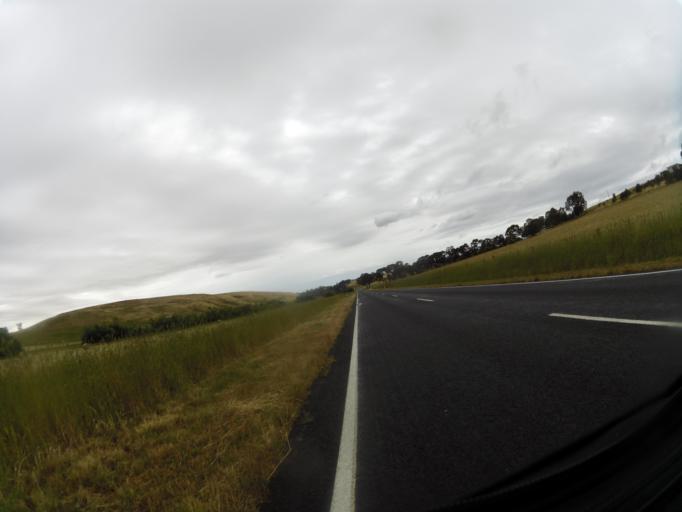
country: AU
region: Victoria
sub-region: Mount Alexander
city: Castlemaine
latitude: -37.1940
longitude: 144.0210
